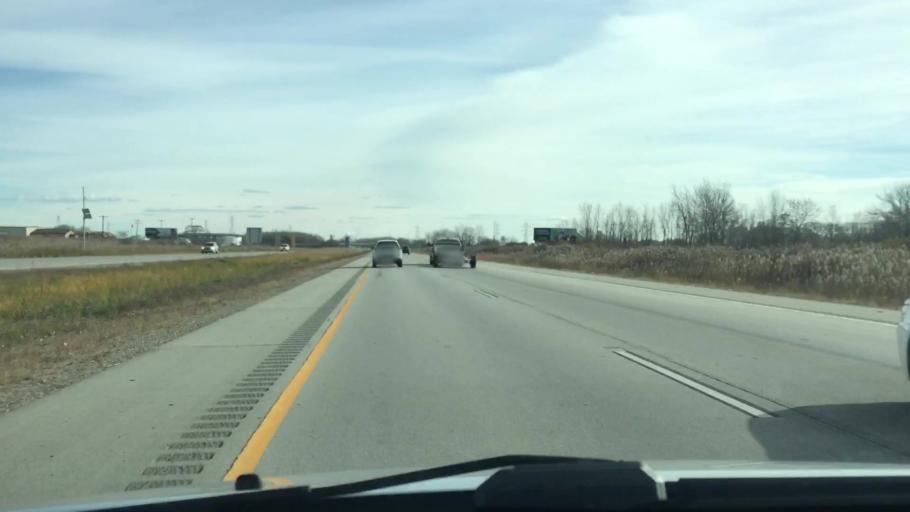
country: US
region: Wisconsin
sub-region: Brown County
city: Green Bay
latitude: 44.5468
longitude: -88.0347
